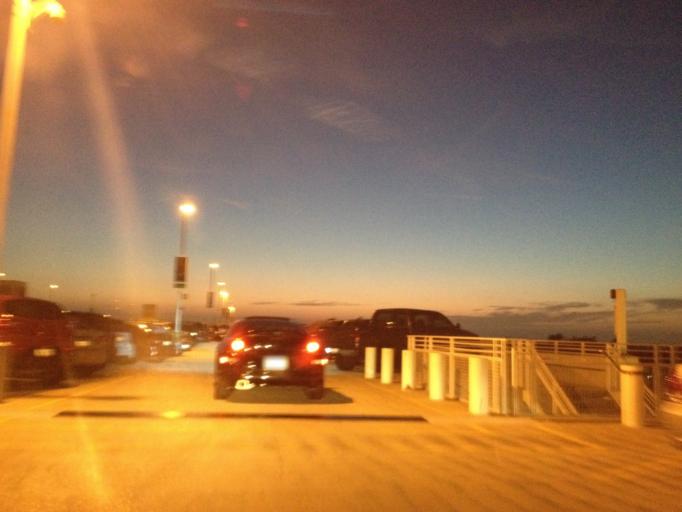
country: US
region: California
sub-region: Orange County
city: Anaheim
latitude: 33.8161
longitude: -117.9251
